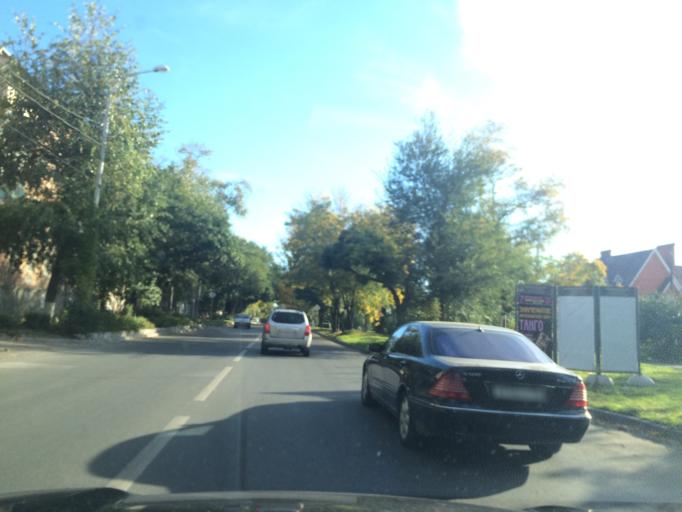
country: RU
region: Rostov
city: Rostov-na-Donu
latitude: 47.2061
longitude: 39.6827
